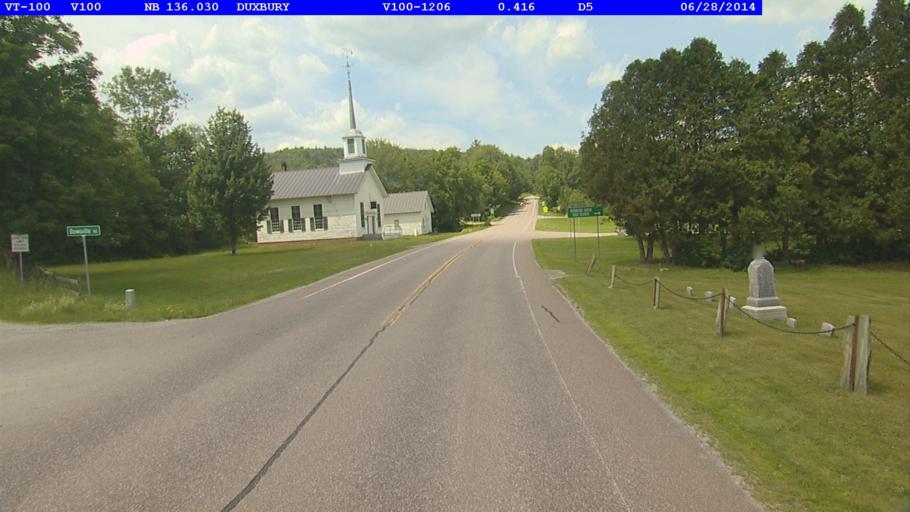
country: US
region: Vermont
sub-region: Washington County
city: Waterbury
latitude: 44.2525
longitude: -72.7879
